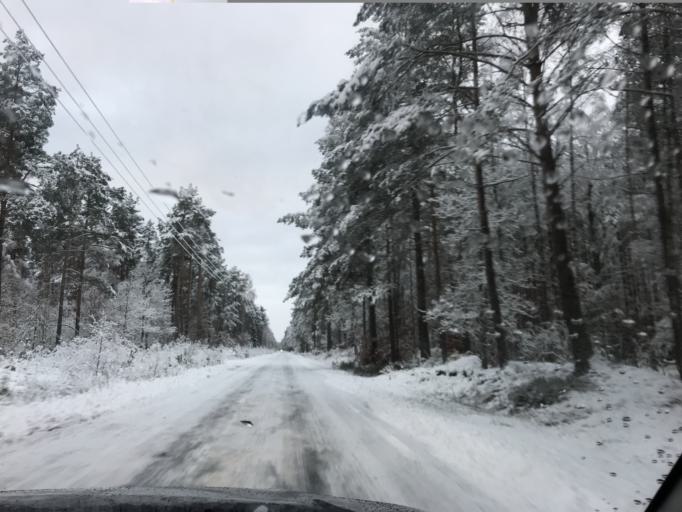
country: PL
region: Pomeranian Voivodeship
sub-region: Powiat bytowski
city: Czarna Dabrowka
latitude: 54.2866
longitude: 17.6006
